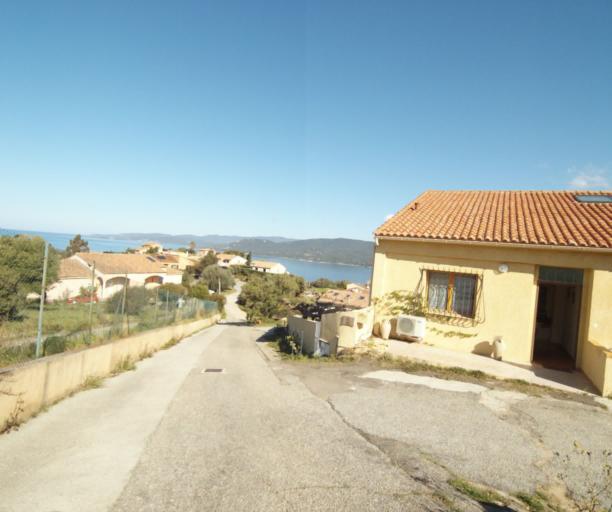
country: FR
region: Corsica
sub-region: Departement de la Corse-du-Sud
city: Propriano
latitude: 41.6681
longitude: 8.9011
